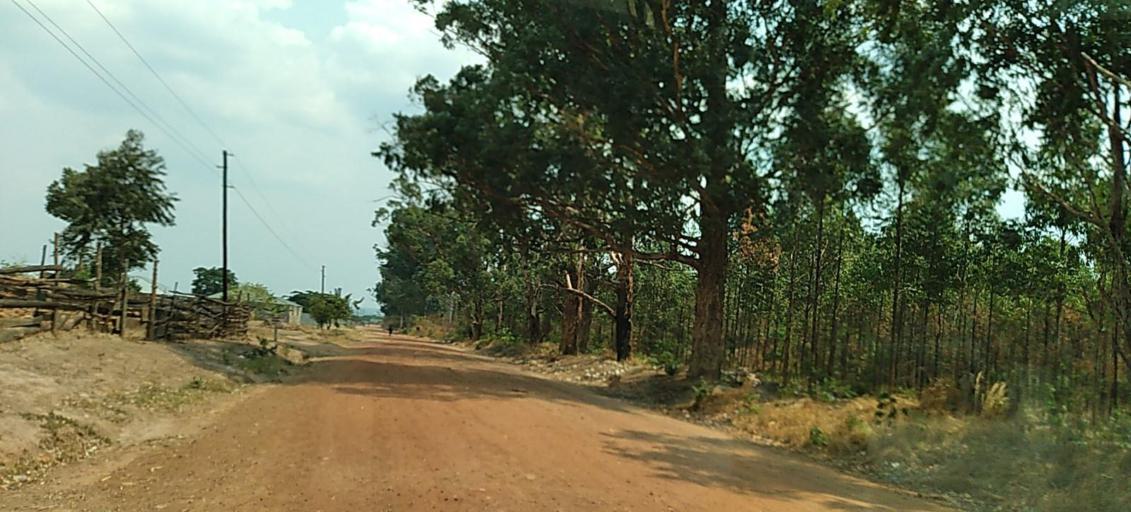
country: ZM
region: Copperbelt
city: Kalulushi
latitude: -12.8470
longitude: 28.0780
